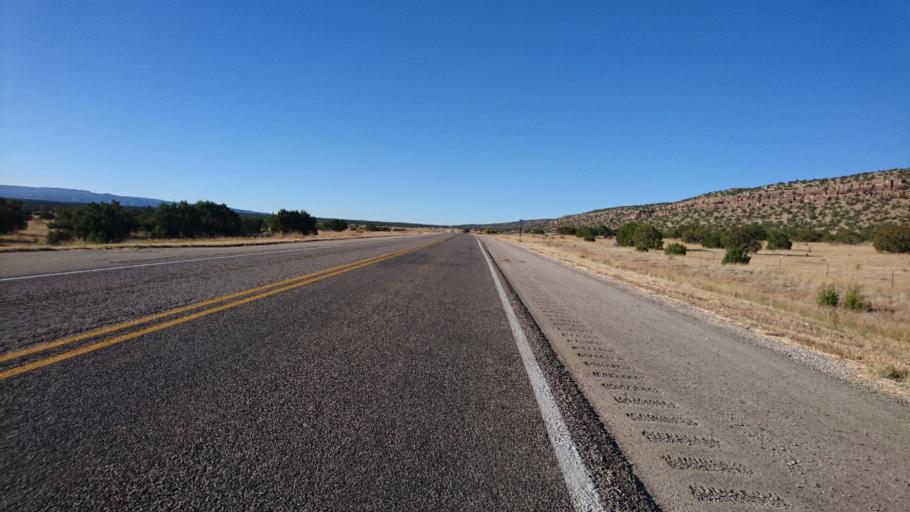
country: US
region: New Mexico
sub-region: Cibola County
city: Grants
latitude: 34.9972
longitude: -107.8973
